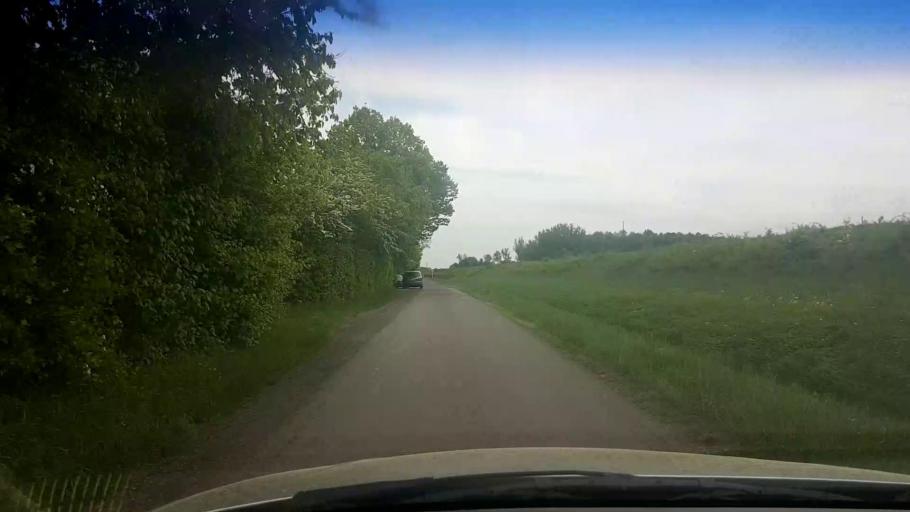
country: DE
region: Bavaria
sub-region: Upper Franconia
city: Bamberg
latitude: 49.8731
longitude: 10.9135
